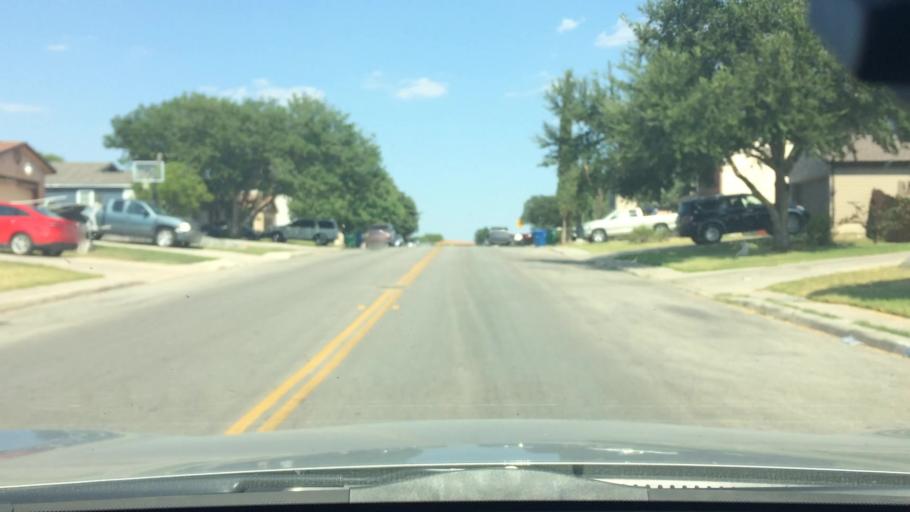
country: US
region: Texas
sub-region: Bexar County
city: Kirby
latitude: 29.4685
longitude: -98.3678
